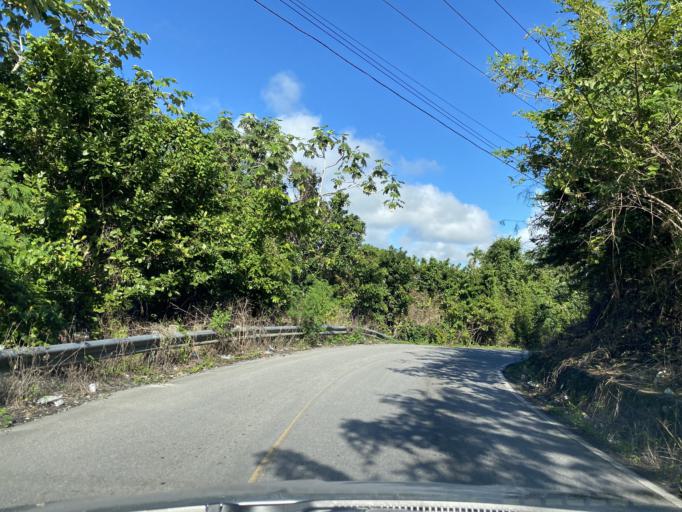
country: DO
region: Samana
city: Sanchez
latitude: 19.2497
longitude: -69.5932
